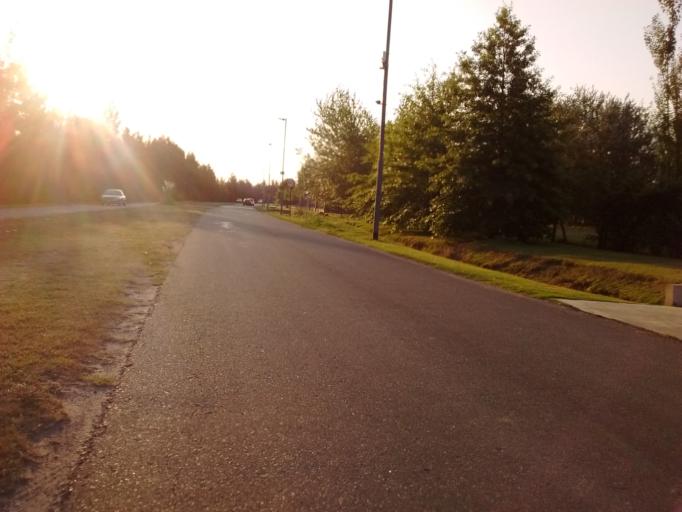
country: AR
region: Santa Fe
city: Funes
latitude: -32.9195
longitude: -60.7676
